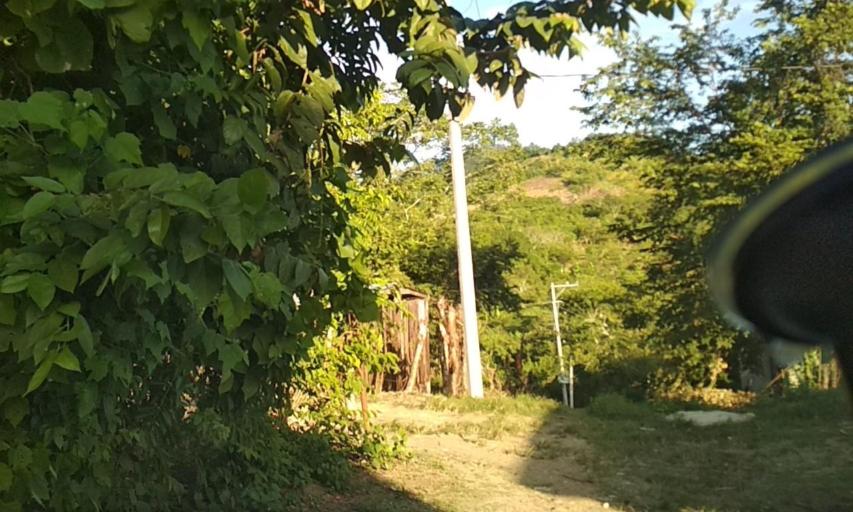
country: MX
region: Veracruz
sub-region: Poza Rica de Hidalgo
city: El Mollejon
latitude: 20.5436
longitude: -97.4065
